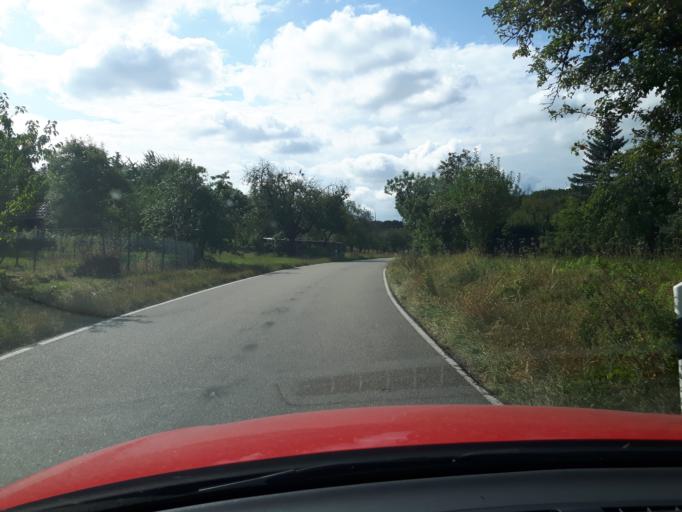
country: DE
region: Baden-Wuerttemberg
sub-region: Regierungsbezirk Stuttgart
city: Nordheim
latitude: 49.1185
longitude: 9.0988
